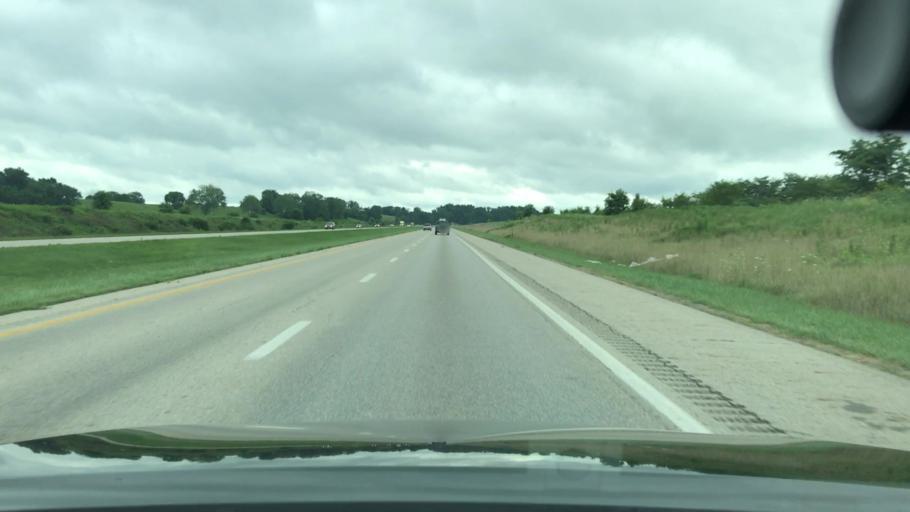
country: US
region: Ohio
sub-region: Ross County
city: Chillicothe
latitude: 39.2887
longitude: -82.8943
